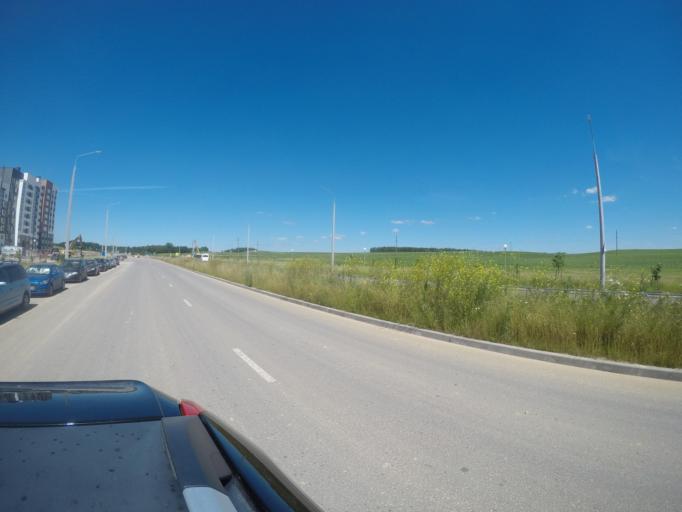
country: BY
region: Grodnenskaya
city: Hrodna
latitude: 53.7222
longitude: 23.8866
